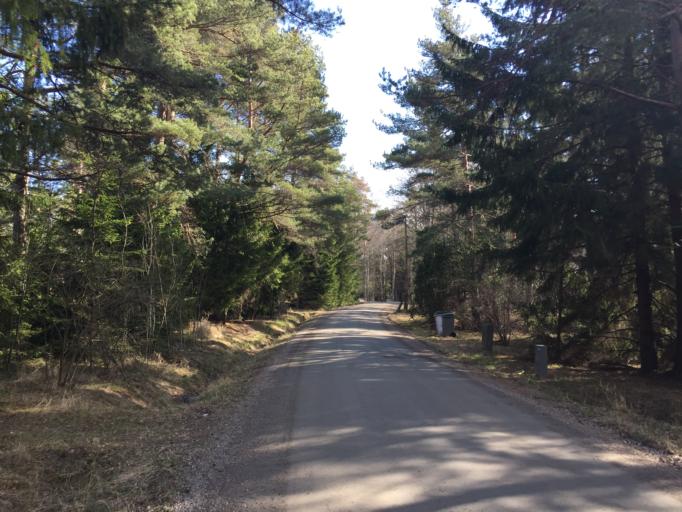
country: SE
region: Stockholm
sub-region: Varmdo Kommun
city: Holo
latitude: 59.2775
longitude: 18.7498
